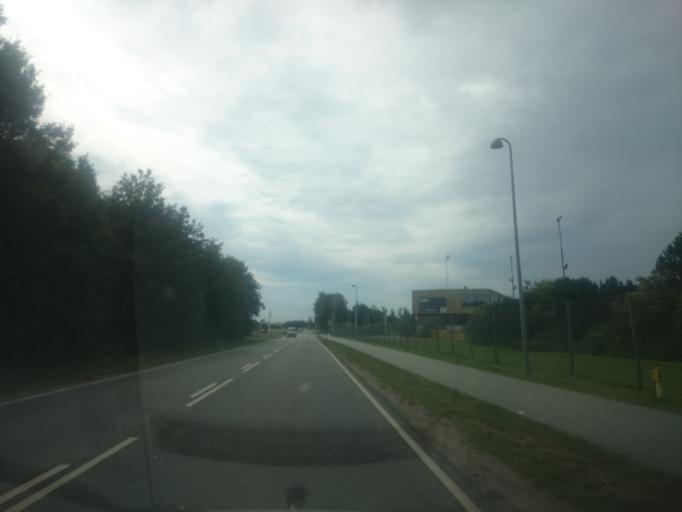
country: DK
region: South Denmark
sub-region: Billund Kommune
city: Billund
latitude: 55.7301
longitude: 9.1329
